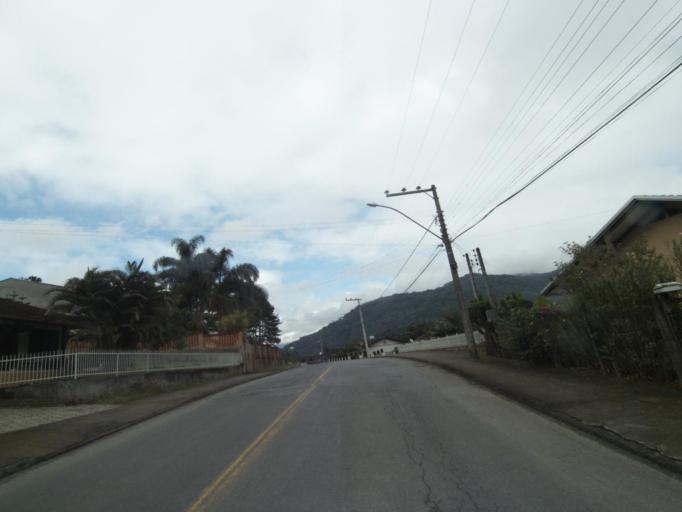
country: BR
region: Santa Catarina
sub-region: Pomerode
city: Pomerode
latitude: -26.7205
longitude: -49.1791
